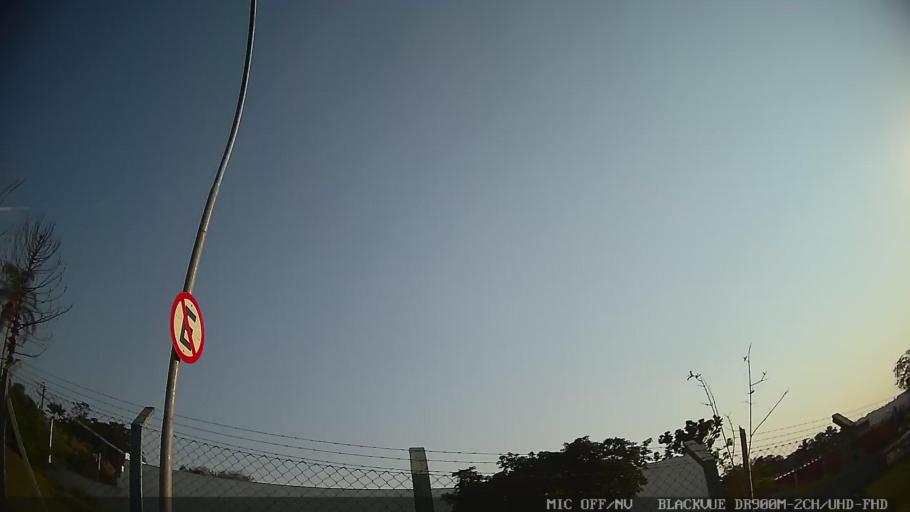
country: BR
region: Sao Paulo
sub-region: Itatiba
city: Itatiba
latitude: -23.0220
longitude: -46.8394
